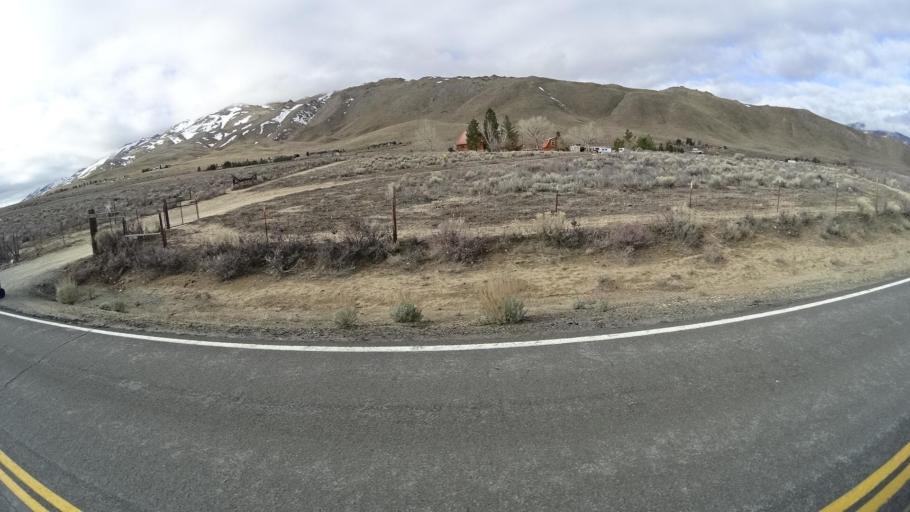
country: US
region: Nevada
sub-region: Washoe County
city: Cold Springs
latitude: 39.8893
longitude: -119.9746
